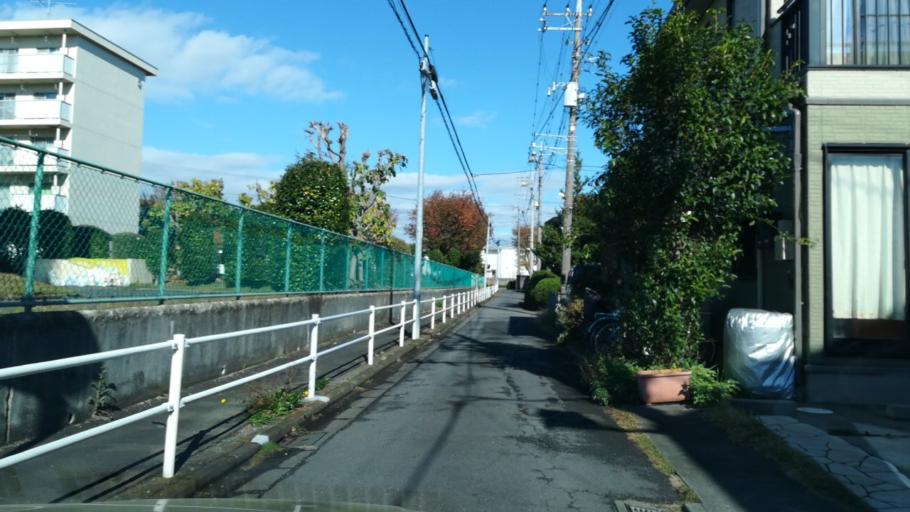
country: JP
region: Tokyo
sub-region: Machida-shi
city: Machida
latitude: 35.5778
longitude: 139.3903
